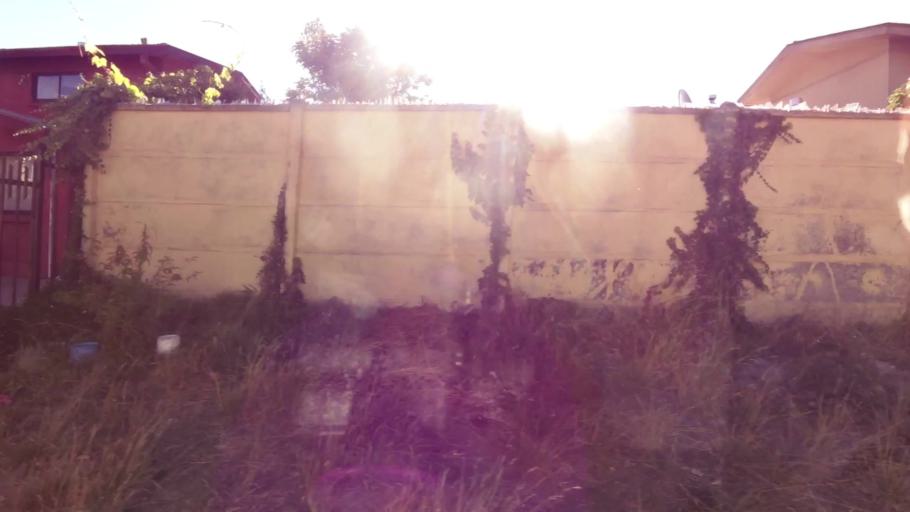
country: CL
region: Biobio
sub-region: Provincia de Concepcion
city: Concepcion
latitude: -36.8407
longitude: -73.1050
